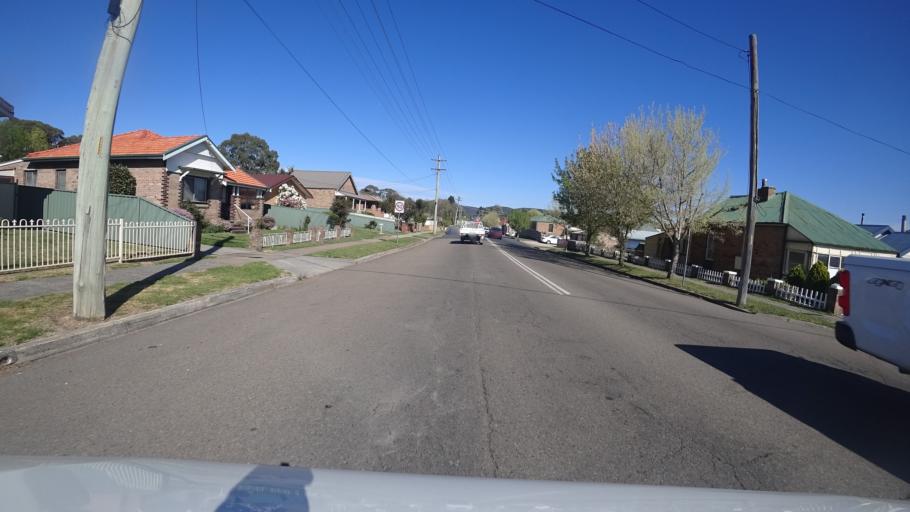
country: AU
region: New South Wales
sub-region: Lithgow
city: Lithgow
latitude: -33.4879
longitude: 150.1460
